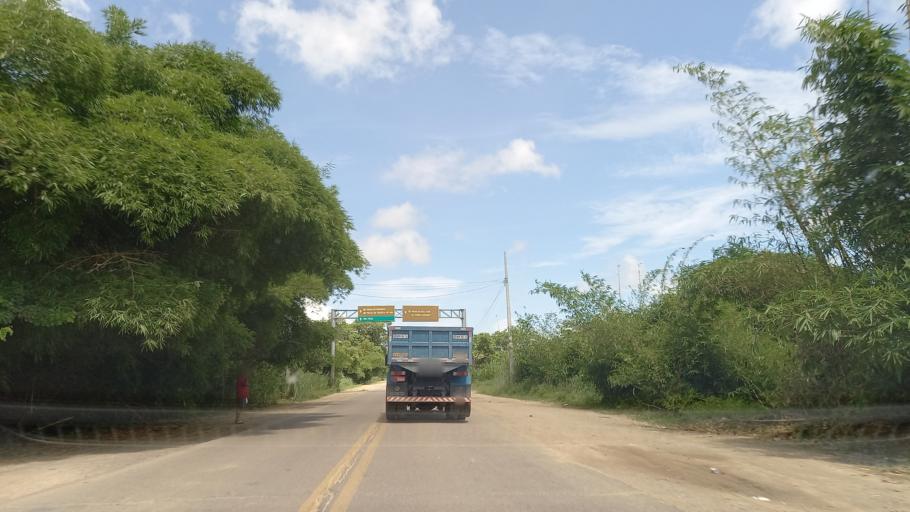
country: BR
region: Pernambuco
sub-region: Barreiros
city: Barreiros
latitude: -8.8088
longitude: -35.1844
